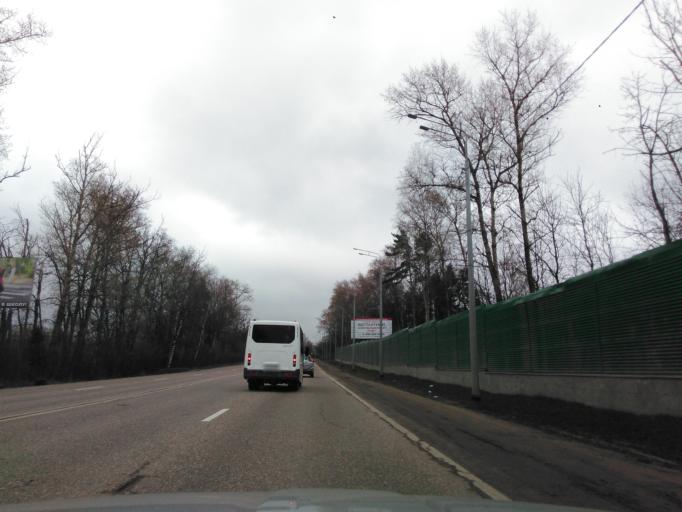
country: RU
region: Moskovskaya
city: Opalikha
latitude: 55.8397
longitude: 37.2323
